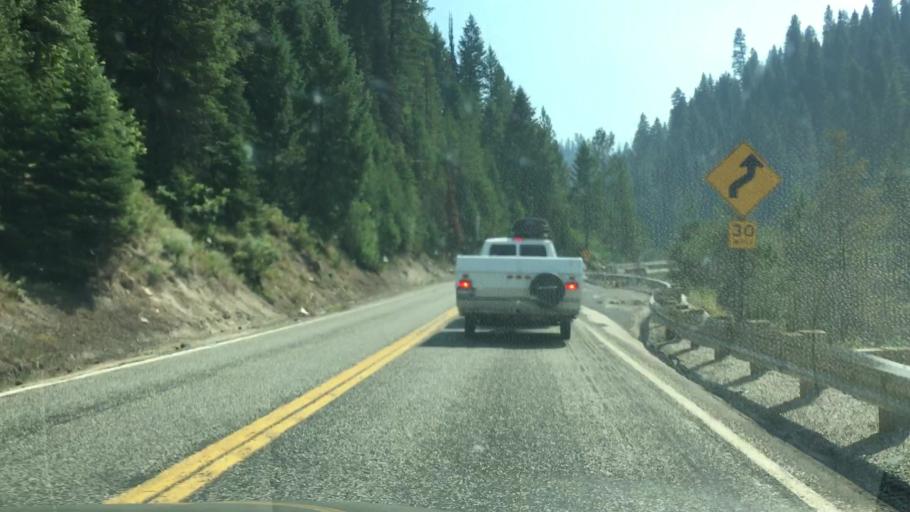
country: US
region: Idaho
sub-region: Valley County
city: Cascade
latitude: 44.3263
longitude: -116.0585
